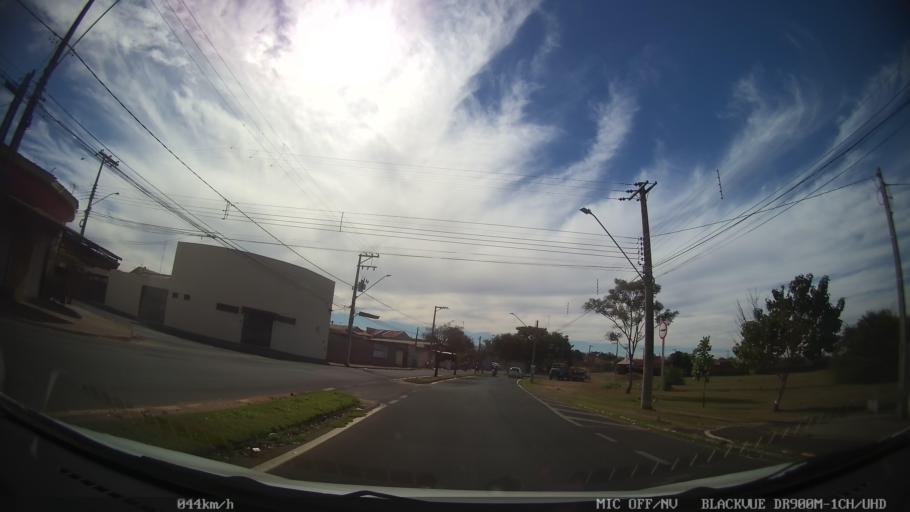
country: BR
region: Sao Paulo
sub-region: Catanduva
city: Catanduva
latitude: -21.1221
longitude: -48.9445
